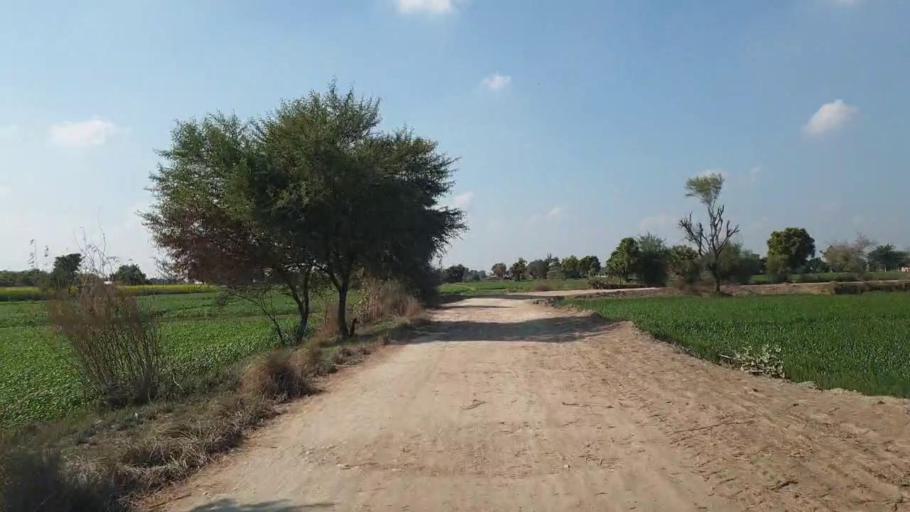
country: PK
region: Sindh
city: Shahpur Chakar
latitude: 26.0797
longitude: 68.5710
